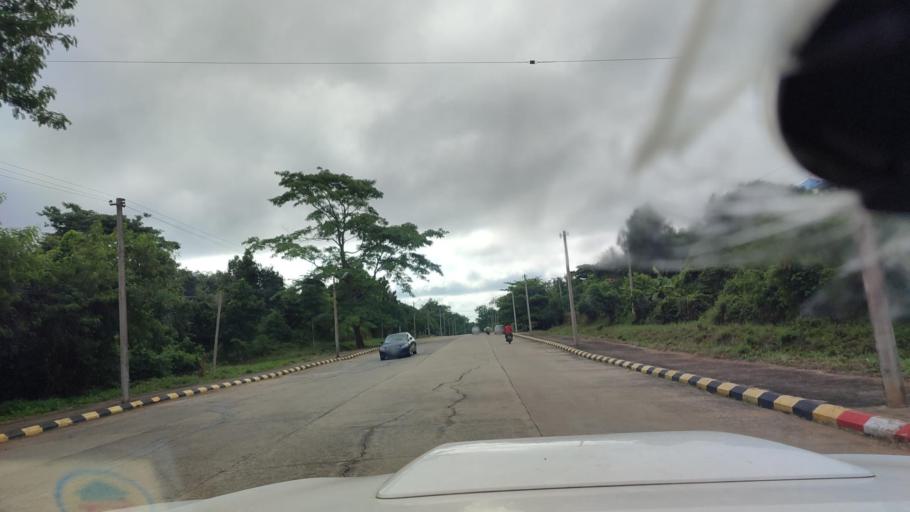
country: MM
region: Mandalay
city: Nay Pyi Taw
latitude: 19.7373
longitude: 96.0635
